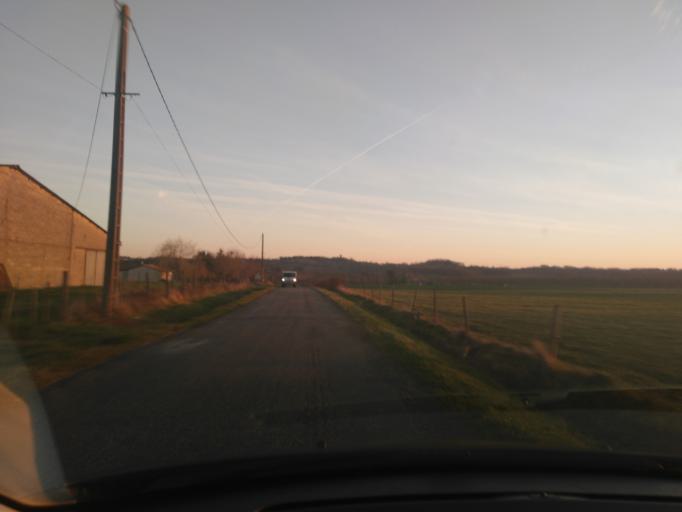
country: FR
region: Aquitaine
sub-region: Departement du Lot-et-Garonne
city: Villeneuve-sur-Lot
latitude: 44.4673
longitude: 0.7184
